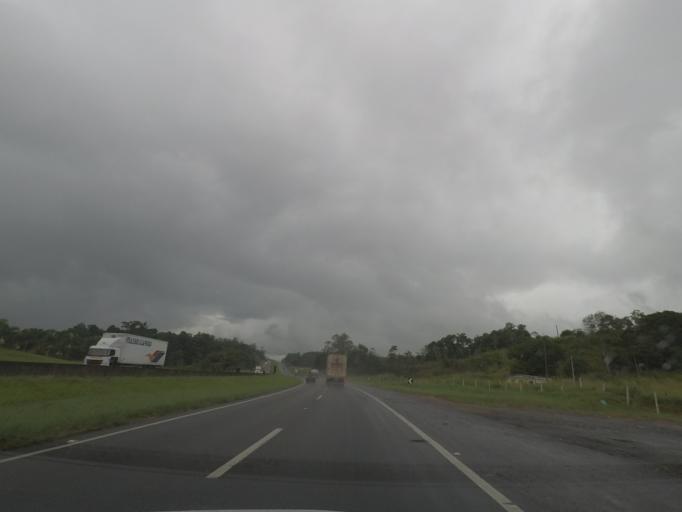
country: BR
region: Sao Paulo
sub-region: Juquia
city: Juquia
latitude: -24.3354
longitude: -47.5929
